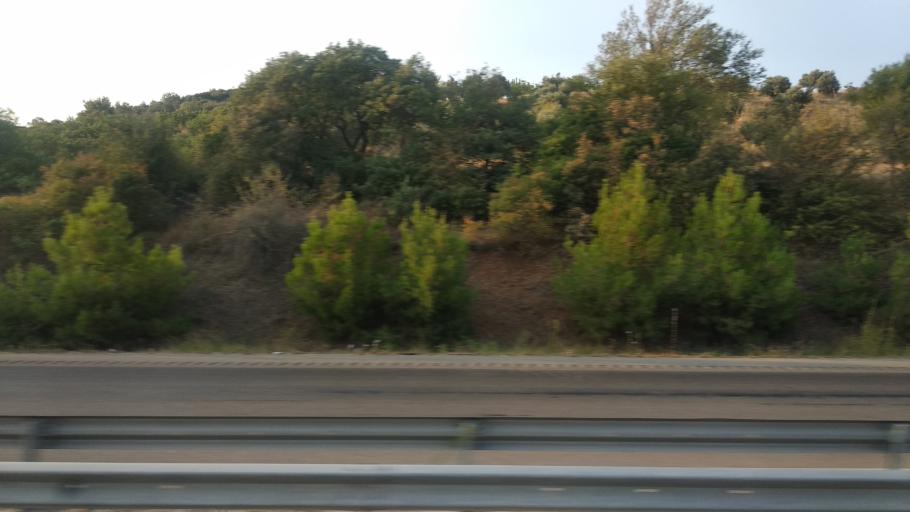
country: TR
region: Manisa
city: Menye
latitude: 38.5667
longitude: 28.5629
